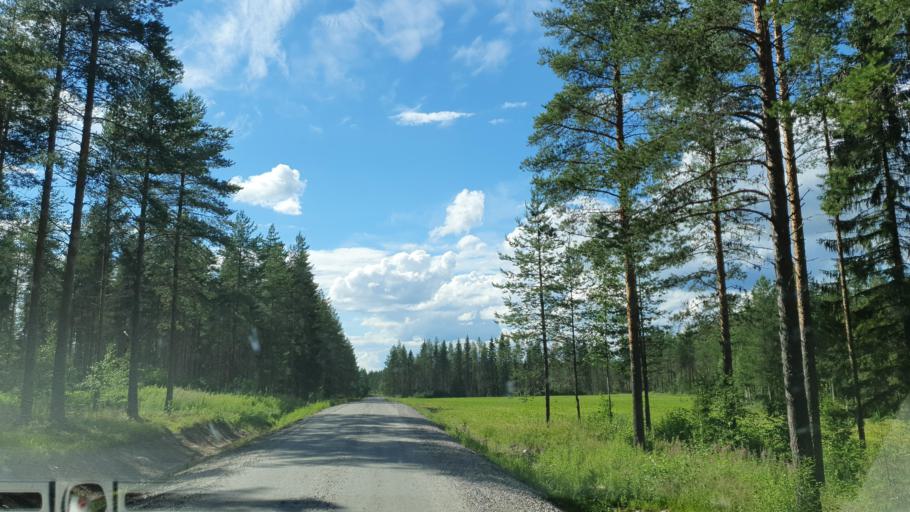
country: FI
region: Kainuu
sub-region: Kehys-Kainuu
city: Kuhmo
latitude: 64.1458
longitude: 29.7744
